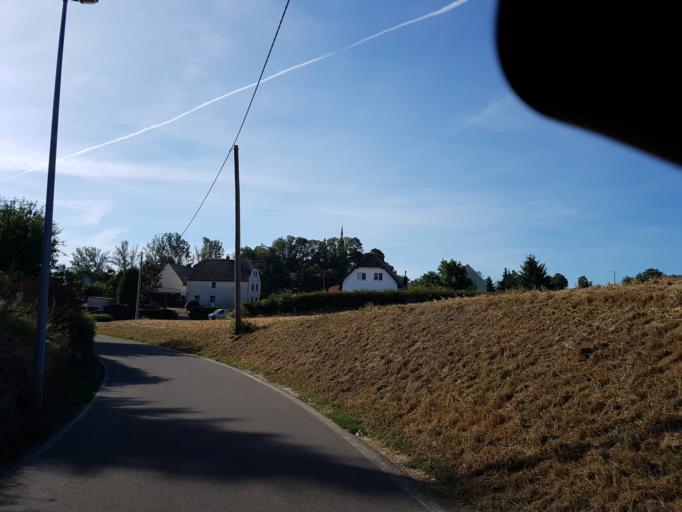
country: DE
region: Saxony
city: Naundorf
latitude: 51.2332
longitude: 13.1273
